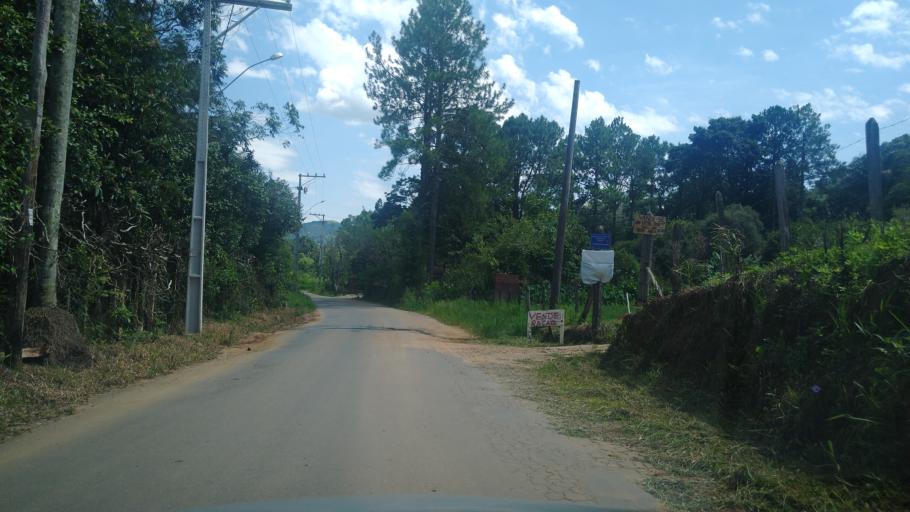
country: BR
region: Minas Gerais
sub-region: Extrema
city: Extrema
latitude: -22.7913
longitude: -46.2882
